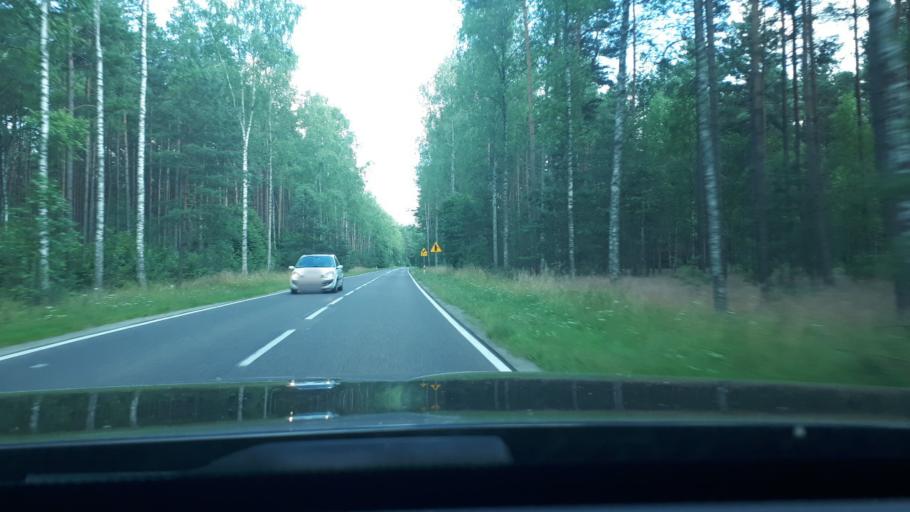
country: PL
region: Warmian-Masurian Voivodeship
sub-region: Powiat olsztynski
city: Stawiguda
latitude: 53.5322
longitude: 20.4370
